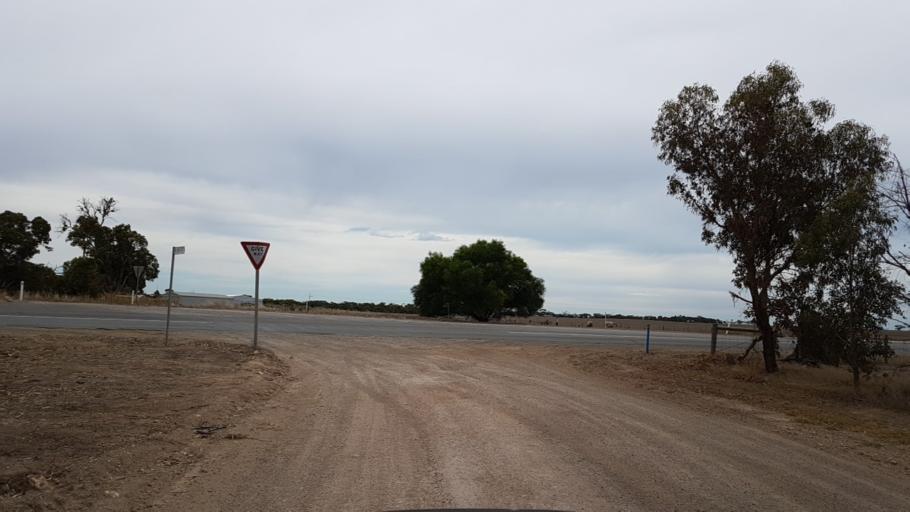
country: AU
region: South Australia
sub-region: Yorke Peninsula
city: Port Victoria
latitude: -34.7737
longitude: 137.6076
